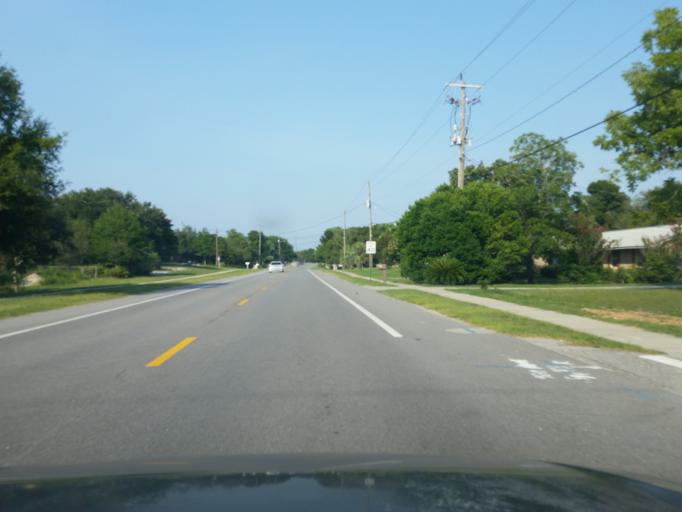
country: US
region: Florida
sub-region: Escambia County
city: Myrtle Grove
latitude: 30.3259
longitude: -87.3828
